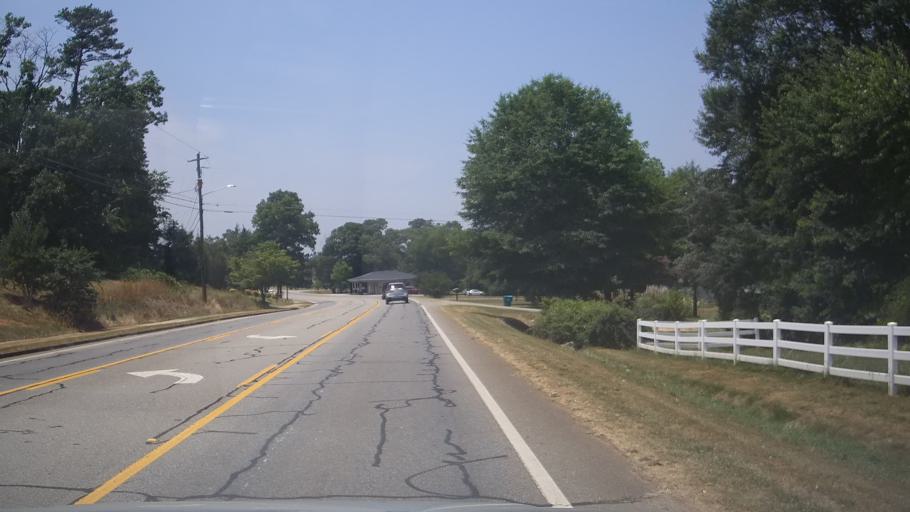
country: US
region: Georgia
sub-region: Hart County
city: Royston
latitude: 34.2853
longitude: -83.1424
